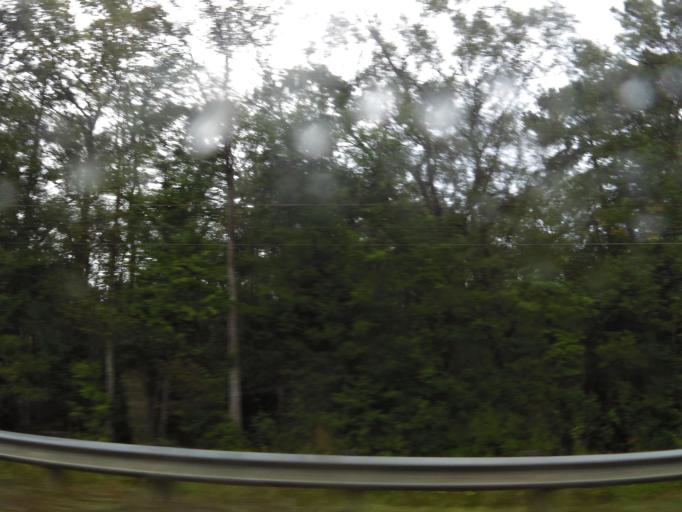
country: US
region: Florida
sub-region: Baker County
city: Macclenny
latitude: 30.3802
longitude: -82.1352
